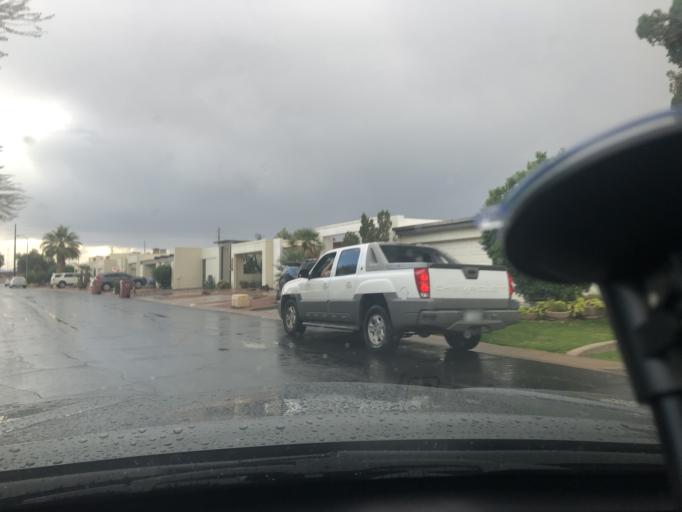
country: US
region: Arizona
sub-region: Maricopa County
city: Scottsdale
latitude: 33.4954
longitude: -111.8942
